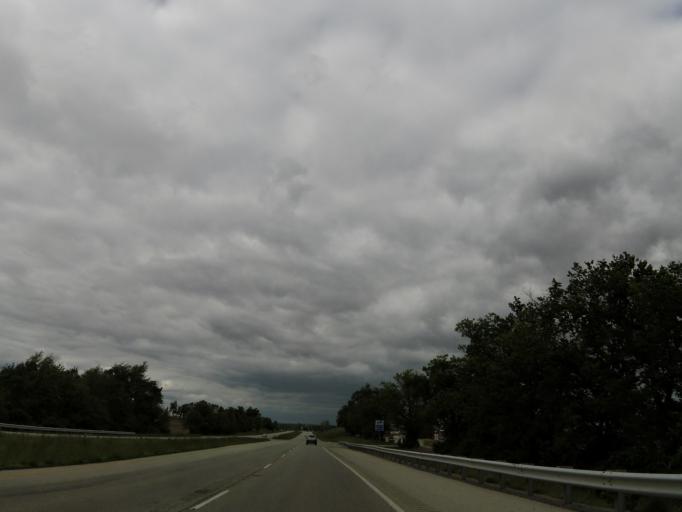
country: US
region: Kentucky
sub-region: Scott County
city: Georgetown
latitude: 38.1904
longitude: -84.5426
